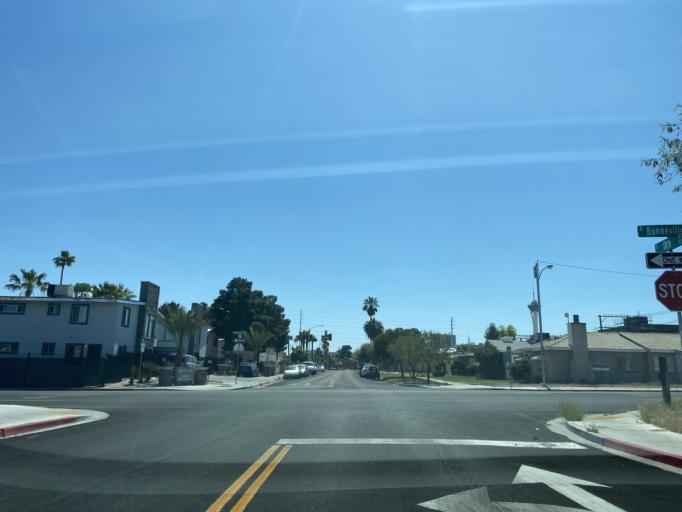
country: US
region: Nevada
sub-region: Clark County
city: Las Vegas
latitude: 36.1607
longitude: -115.1375
